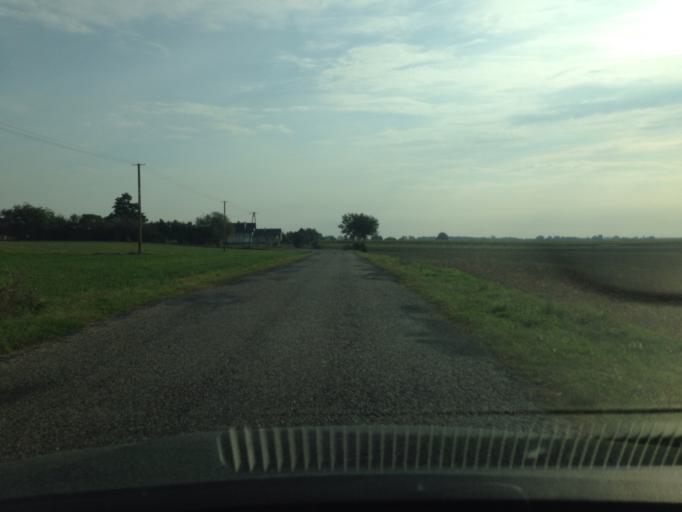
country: PL
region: Kujawsko-Pomorskie
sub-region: Powiat brodnicki
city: Gorzno
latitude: 53.2012
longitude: 19.5991
